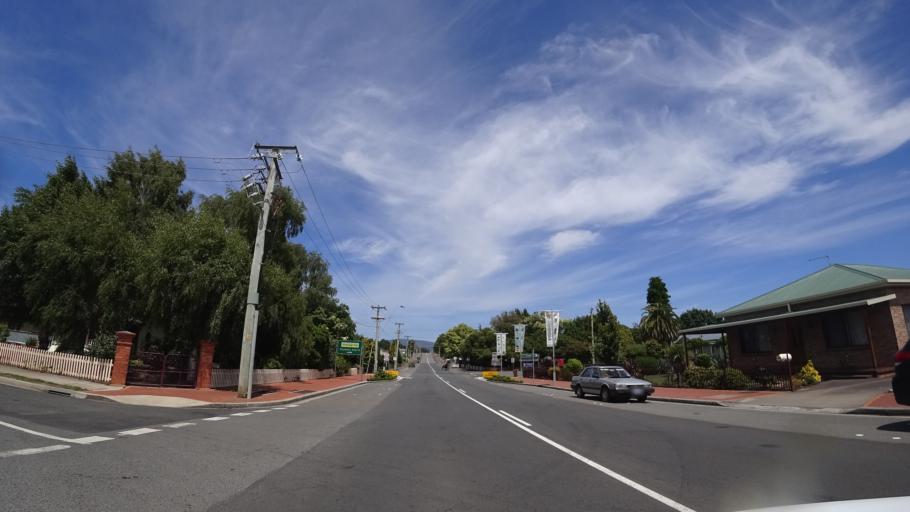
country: AU
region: Tasmania
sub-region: Dorset
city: Scottsdale
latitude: -41.1624
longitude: 147.5145
